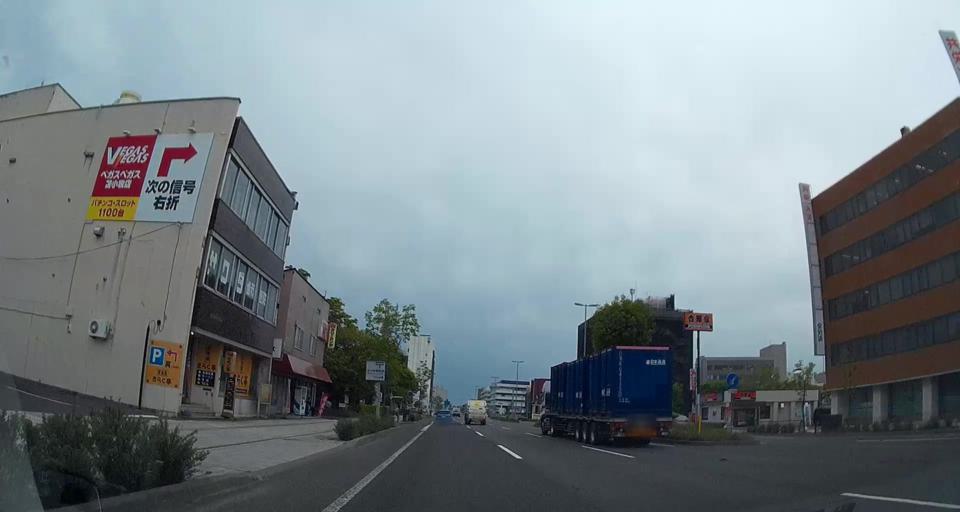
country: JP
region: Hokkaido
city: Tomakomai
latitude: 42.6354
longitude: 141.6057
